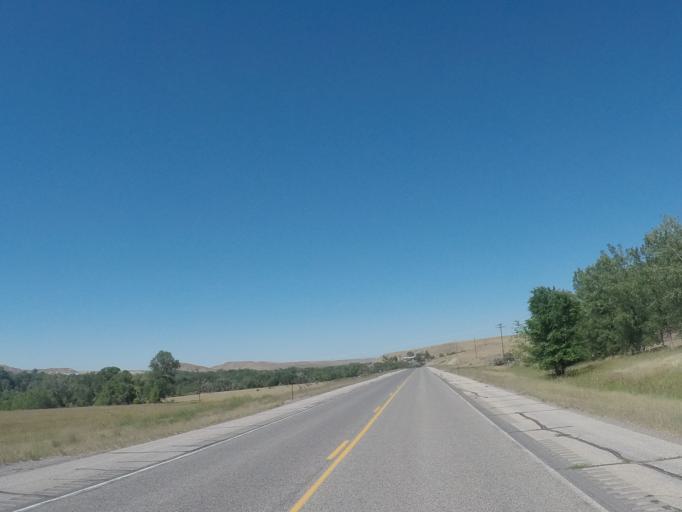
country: US
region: Wyoming
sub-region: Big Horn County
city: Greybull
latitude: 44.5467
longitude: -107.7653
